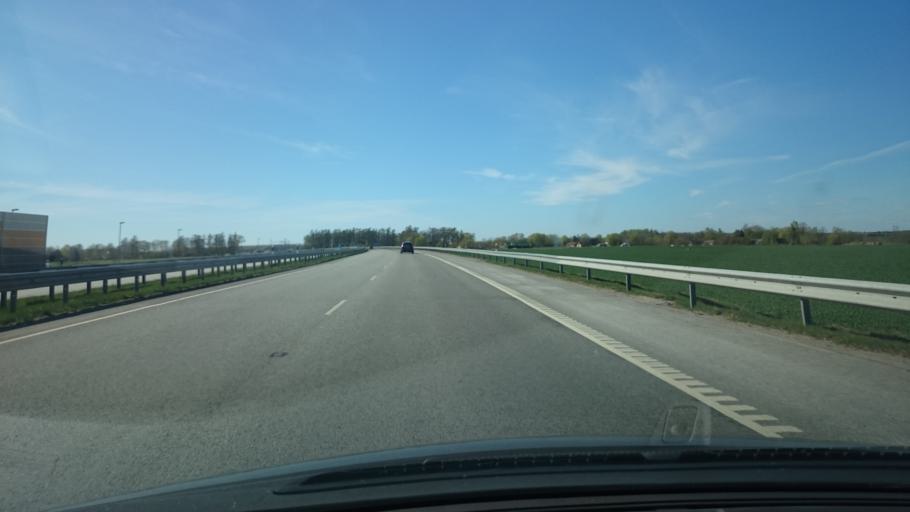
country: EE
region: Ida-Virumaa
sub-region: Johvi vald
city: Johvi
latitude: 59.3794
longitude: 27.3725
